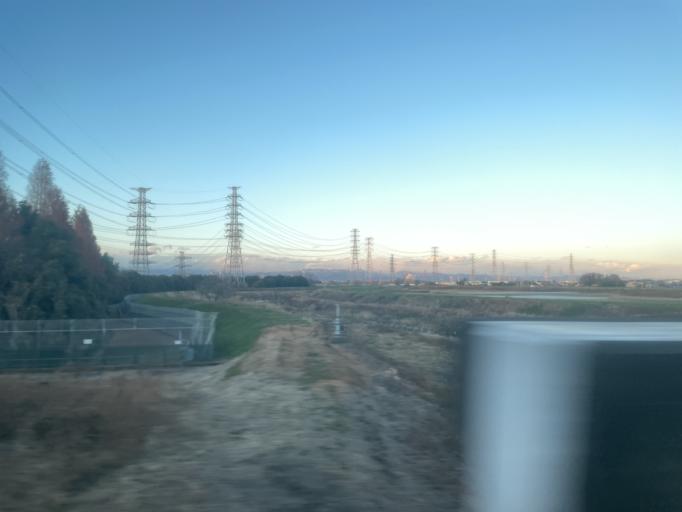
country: JP
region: Saitama
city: Honjo
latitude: 36.2171
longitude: 139.2148
